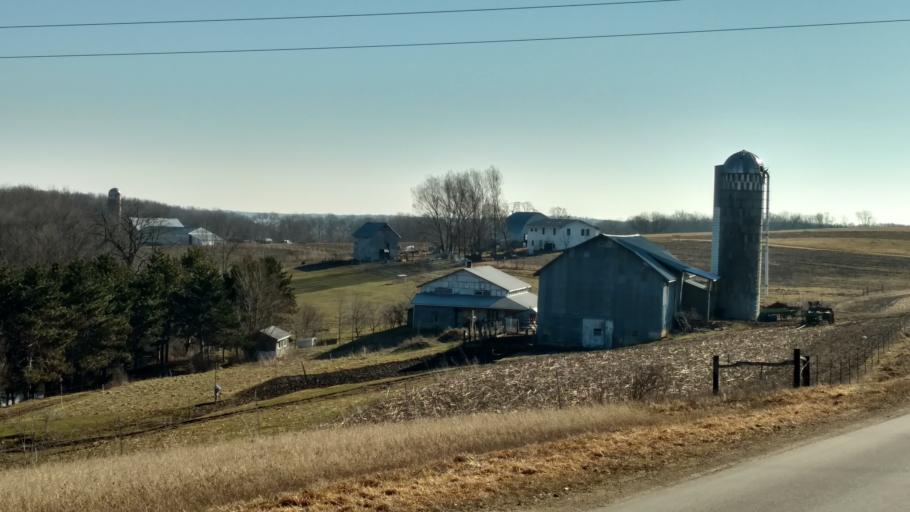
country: US
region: Wisconsin
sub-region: Vernon County
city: Hillsboro
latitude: 43.6061
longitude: -90.4328
